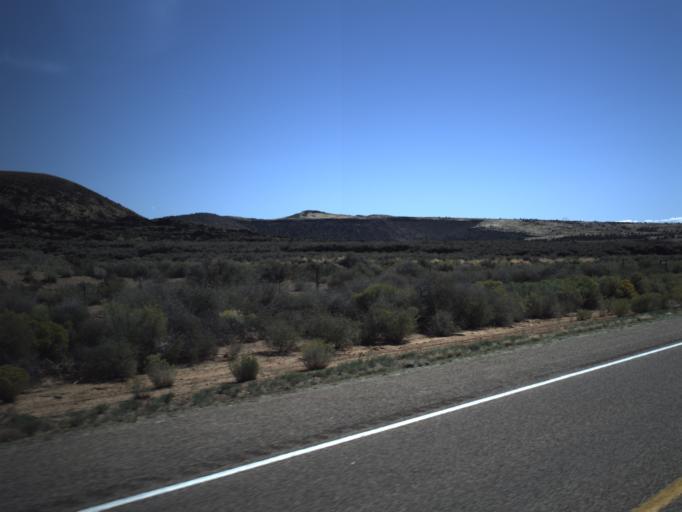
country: US
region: Utah
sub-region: Washington County
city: Ivins
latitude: 37.2582
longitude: -113.6336
